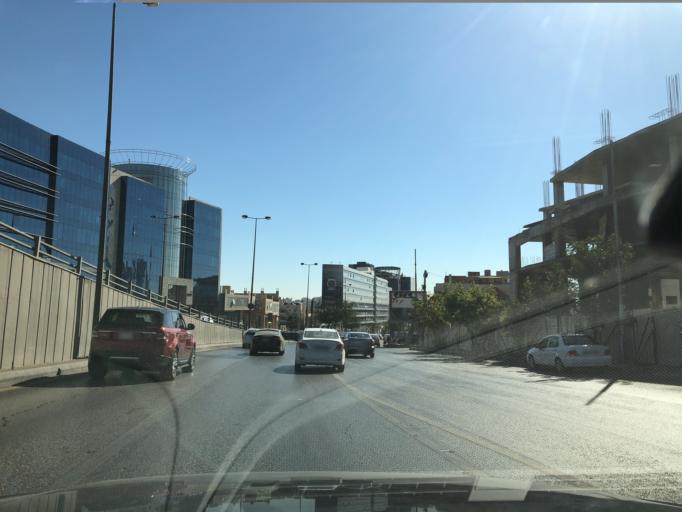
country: JO
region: Amman
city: Wadi as Sir
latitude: 31.9764
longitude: 35.8549
